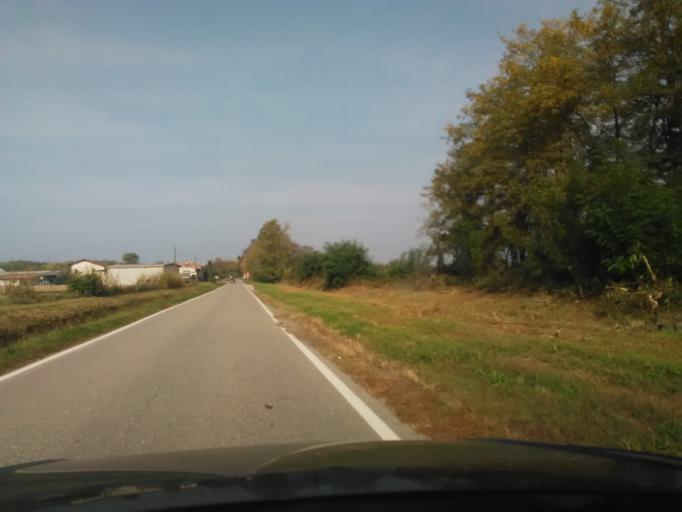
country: IT
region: Piedmont
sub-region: Provincia di Vercelli
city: Santhia
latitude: 45.3572
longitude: 8.1538
